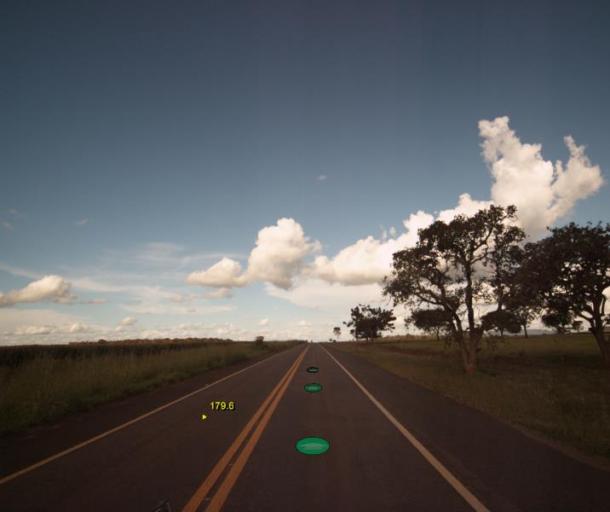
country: BR
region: Goias
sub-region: Itaberai
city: Itaberai
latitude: -15.9852
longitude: -49.7032
